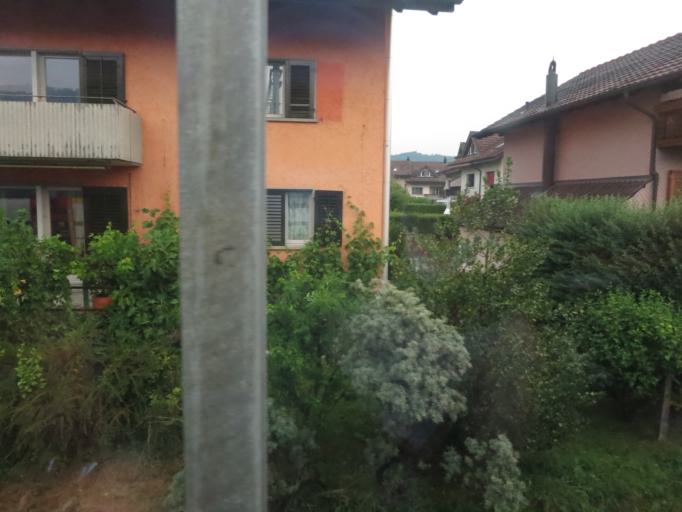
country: CH
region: Schwyz
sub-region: Bezirk March
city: Schubelbach
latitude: 47.1830
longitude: 8.8957
